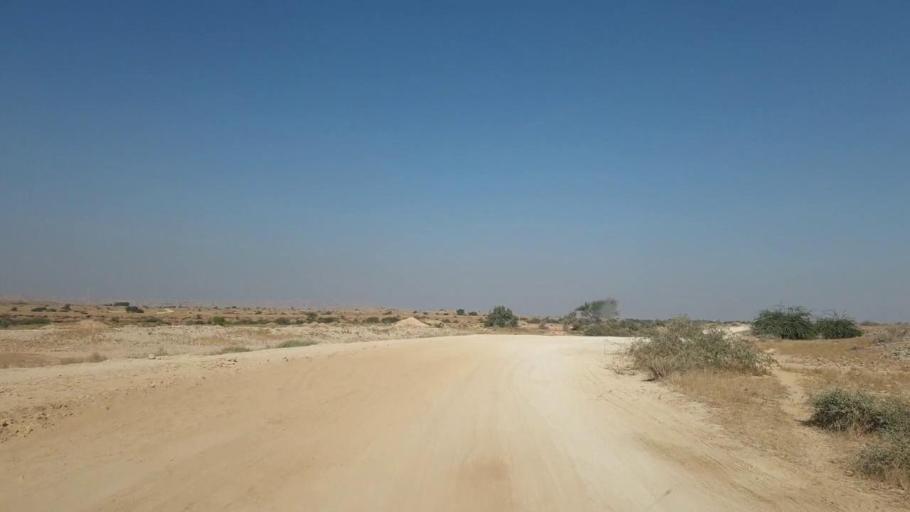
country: PK
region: Sindh
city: Thatta
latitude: 25.2257
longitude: 67.8021
